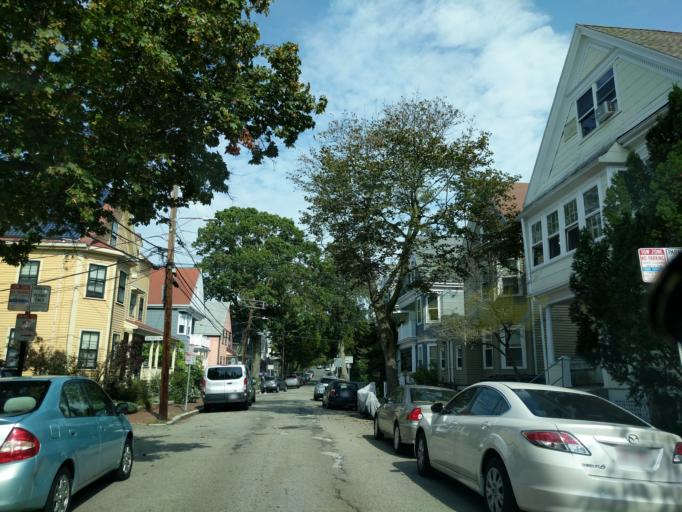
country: US
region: Massachusetts
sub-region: Middlesex County
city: Arlington
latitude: 42.3992
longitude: -71.1305
